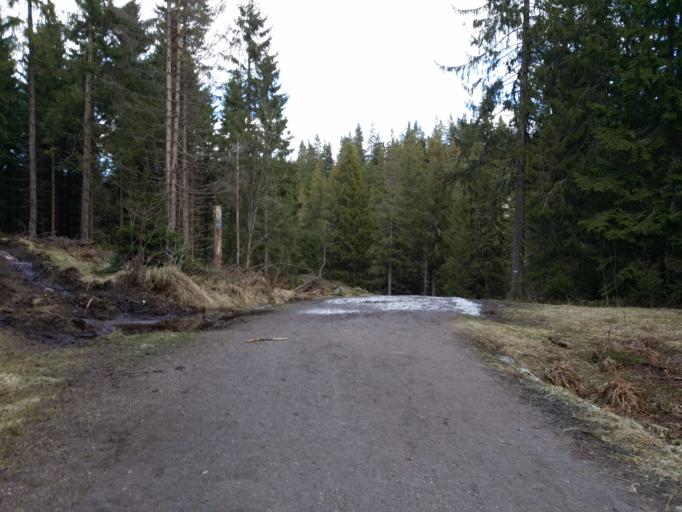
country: NO
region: Oslo
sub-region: Oslo
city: Sjolyststranda
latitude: 59.9868
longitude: 10.6879
